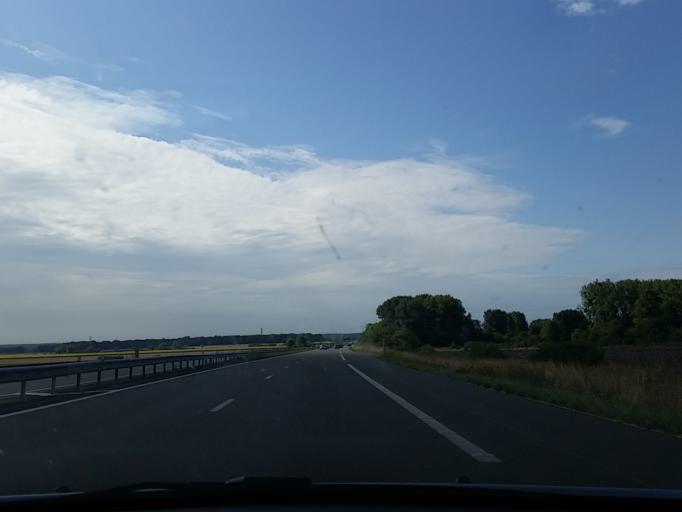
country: FR
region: Centre
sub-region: Departement du Cher
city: Chateauneuf-sur-Cher
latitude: 46.8215
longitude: 2.4128
